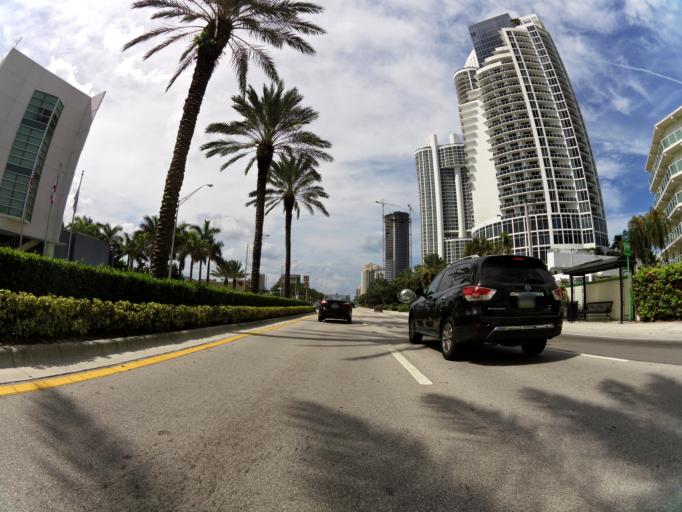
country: US
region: Florida
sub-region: Miami-Dade County
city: Sunny Isles Beach
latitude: 25.9423
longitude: -80.1213
